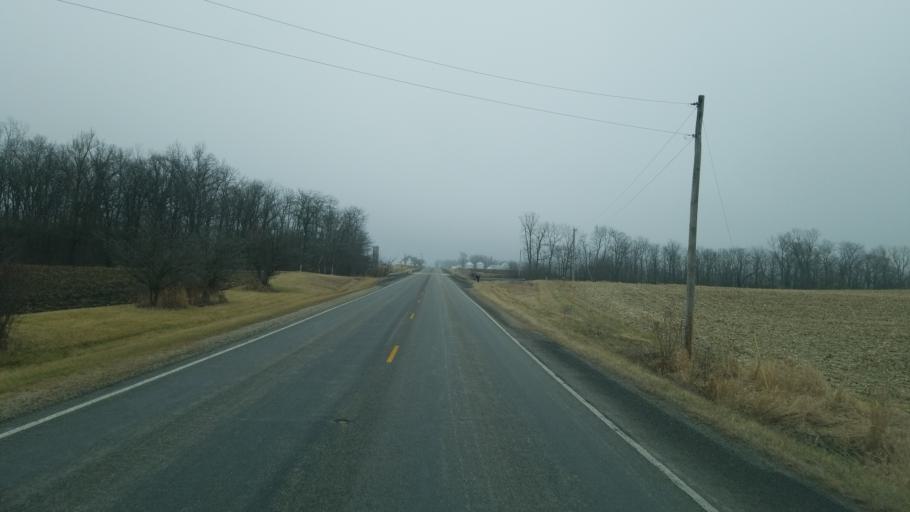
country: US
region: Indiana
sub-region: Adams County
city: Geneva
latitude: 40.5474
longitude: -85.0212
